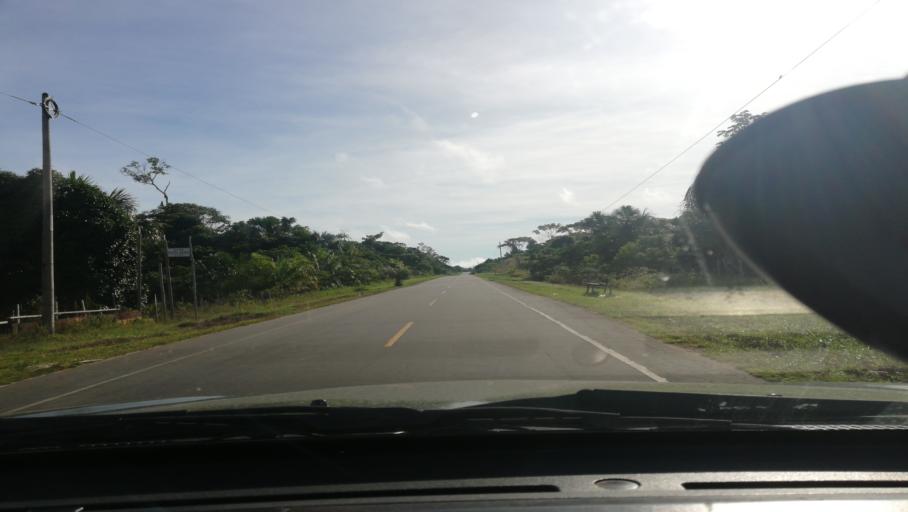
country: PE
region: Loreto
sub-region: Provincia de Loreto
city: Nauta
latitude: -4.3624
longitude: -73.5570
